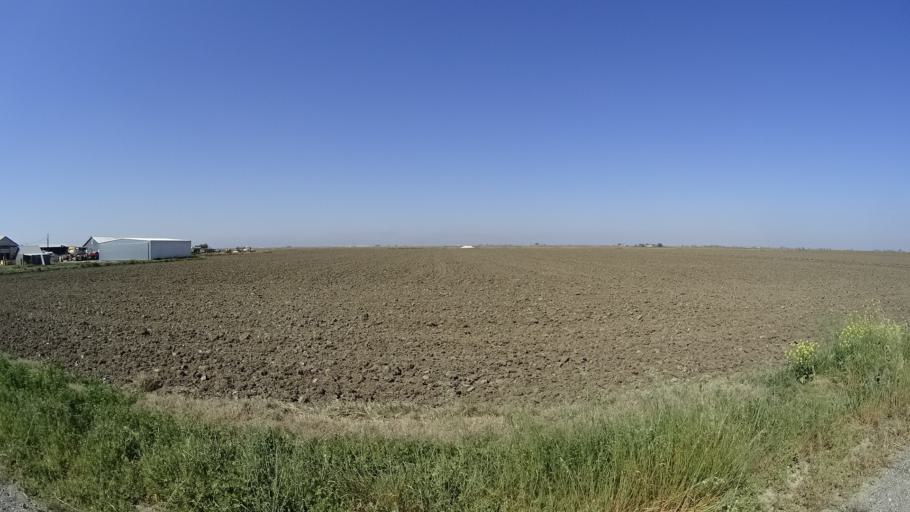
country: US
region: California
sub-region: Glenn County
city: Willows
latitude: 39.4826
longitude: -122.0556
